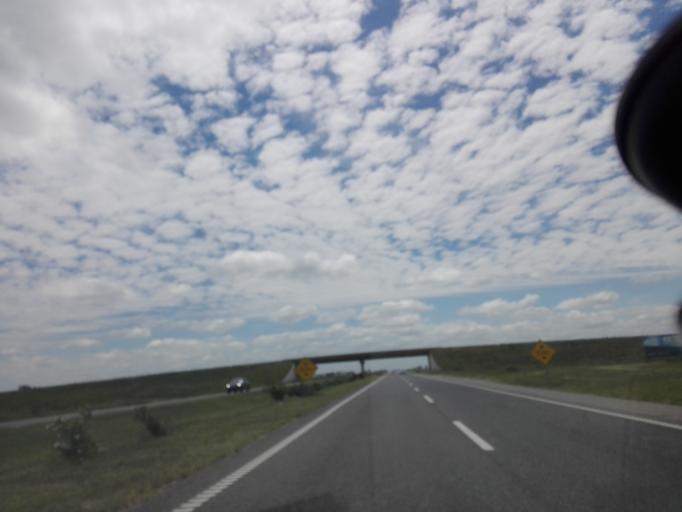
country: AR
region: Cordoba
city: Oliva
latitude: -31.9907
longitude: -63.5624
